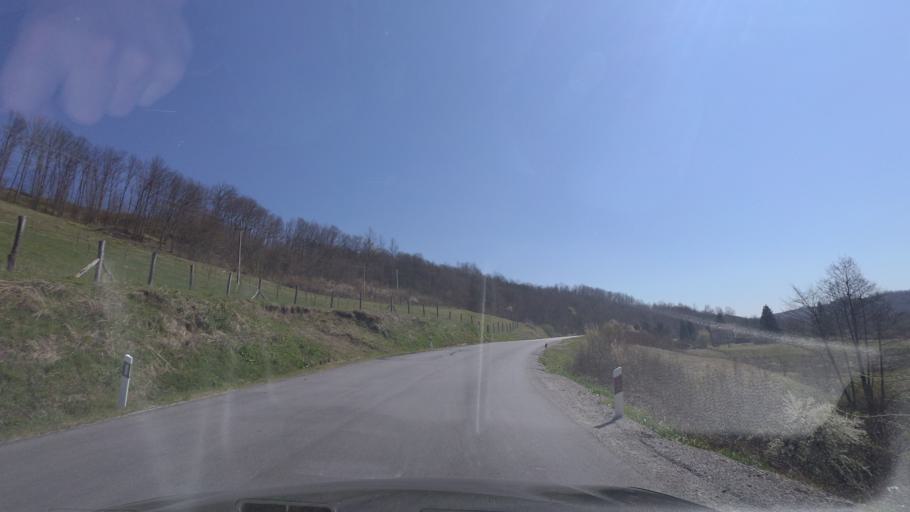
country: HR
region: Karlovacka
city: Vojnic
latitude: 45.3563
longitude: 15.6742
